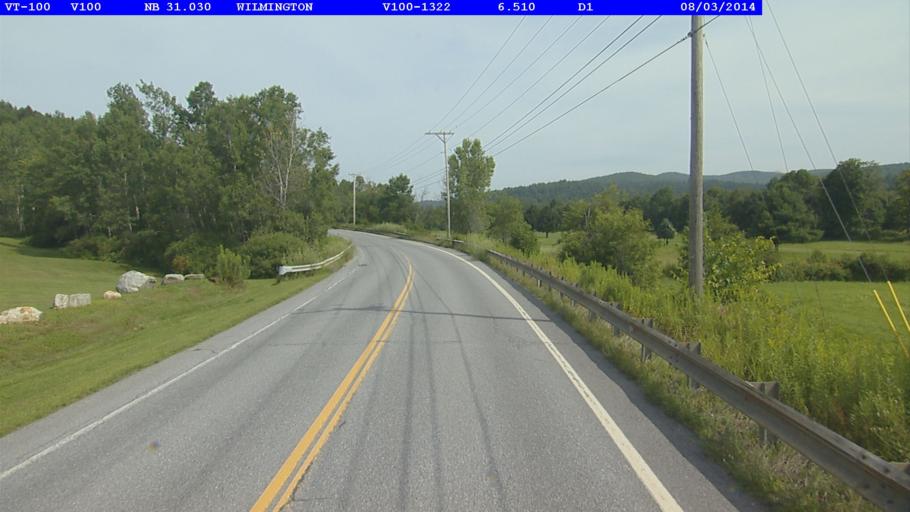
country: US
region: Vermont
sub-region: Windham County
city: Dover
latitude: 42.9151
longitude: -72.8392
